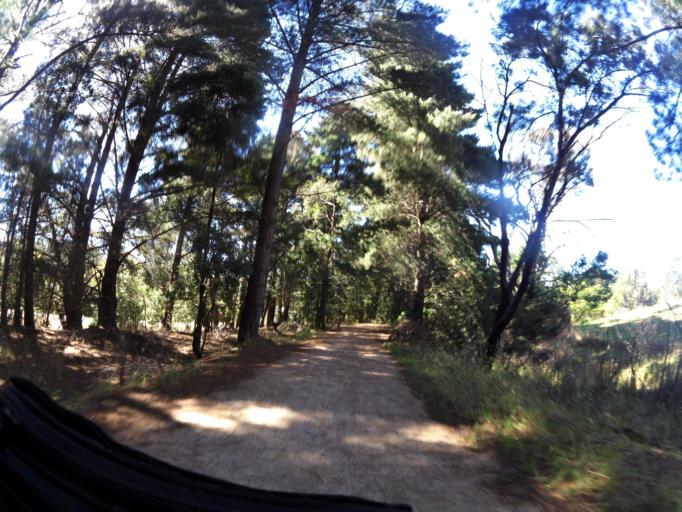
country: AU
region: Victoria
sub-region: Ballarat North
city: Delacombe
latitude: -37.6806
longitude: 143.5655
